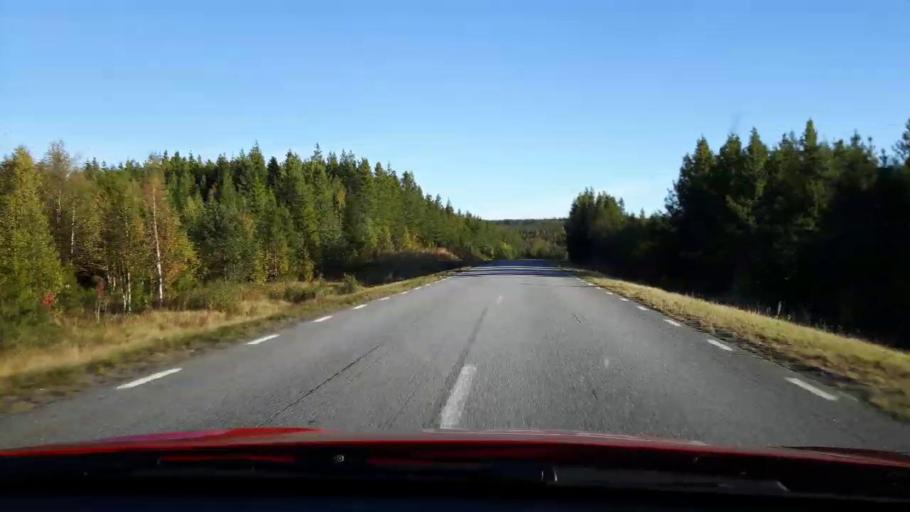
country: SE
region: Jaemtland
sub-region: OEstersunds Kommun
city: Lit
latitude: 63.7704
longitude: 14.7187
